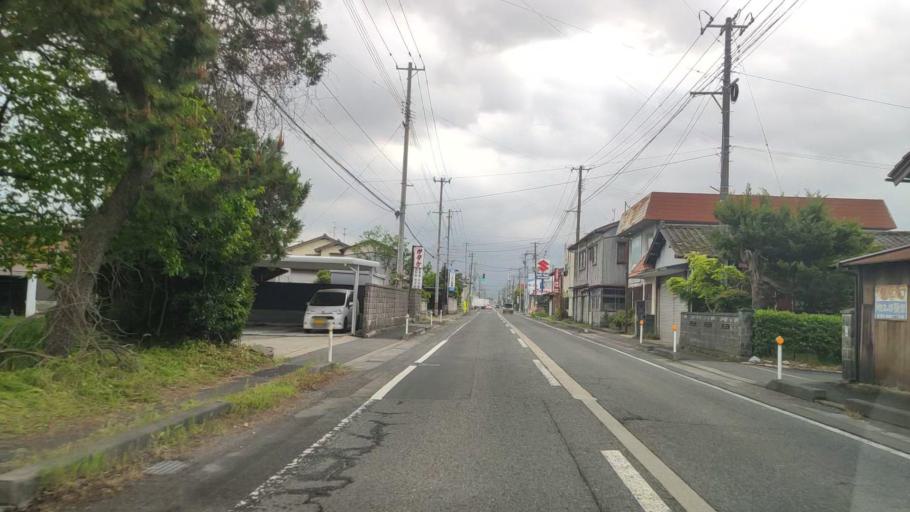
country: JP
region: Niigata
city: Gosen
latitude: 37.7353
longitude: 139.1923
